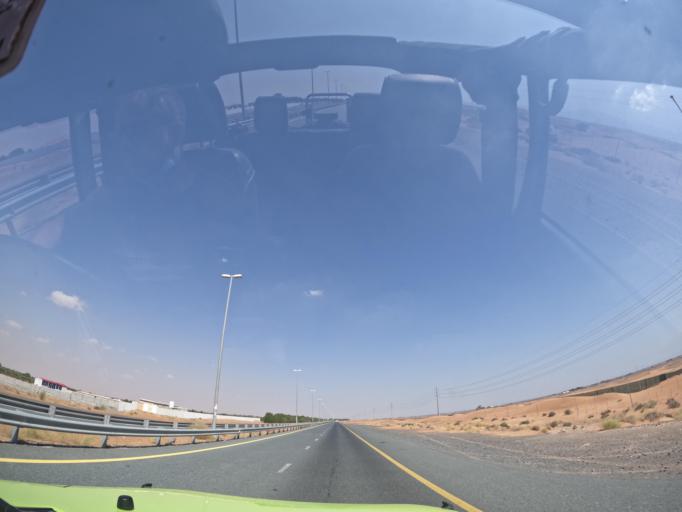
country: AE
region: Ash Shariqah
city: Adh Dhayd
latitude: 24.8346
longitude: 55.7872
